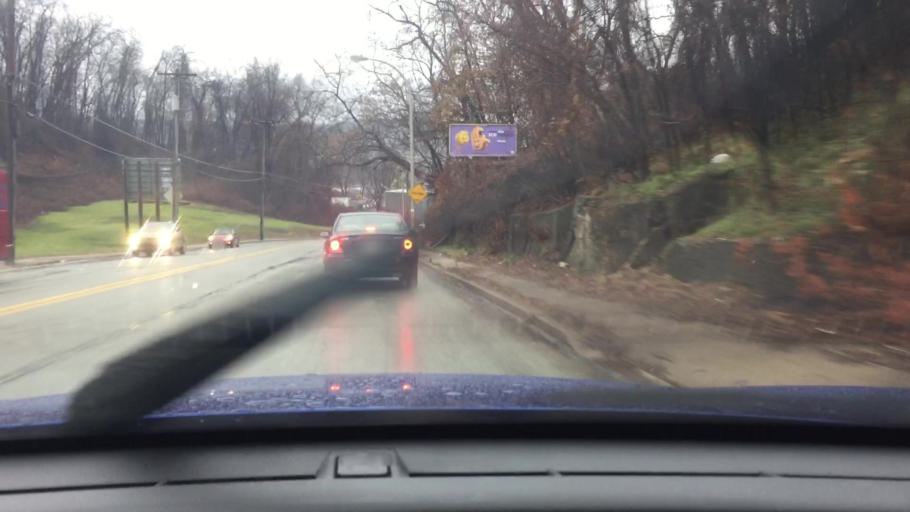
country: US
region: Pennsylvania
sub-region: Allegheny County
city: Bloomfield
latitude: 40.4532
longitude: -79.9652
